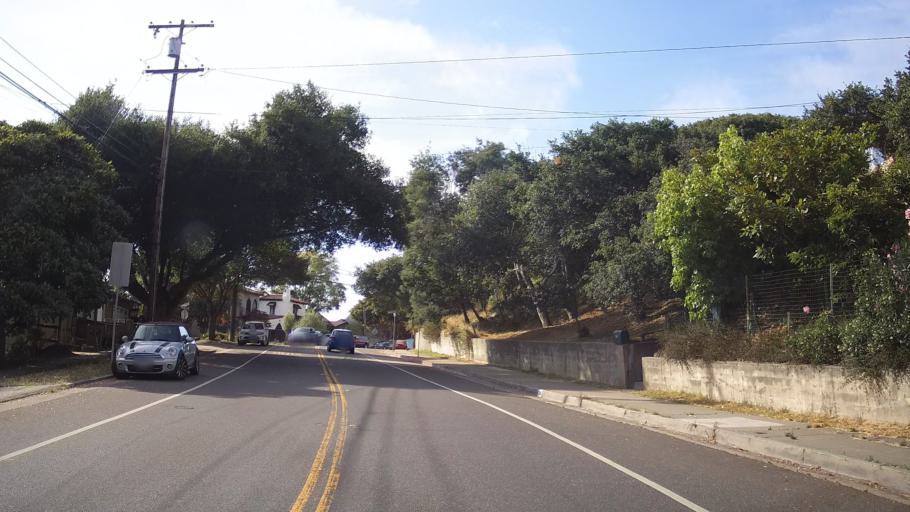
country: US
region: California
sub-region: Contra Costa County
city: Kensington
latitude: 37.8948
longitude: -122.2687
